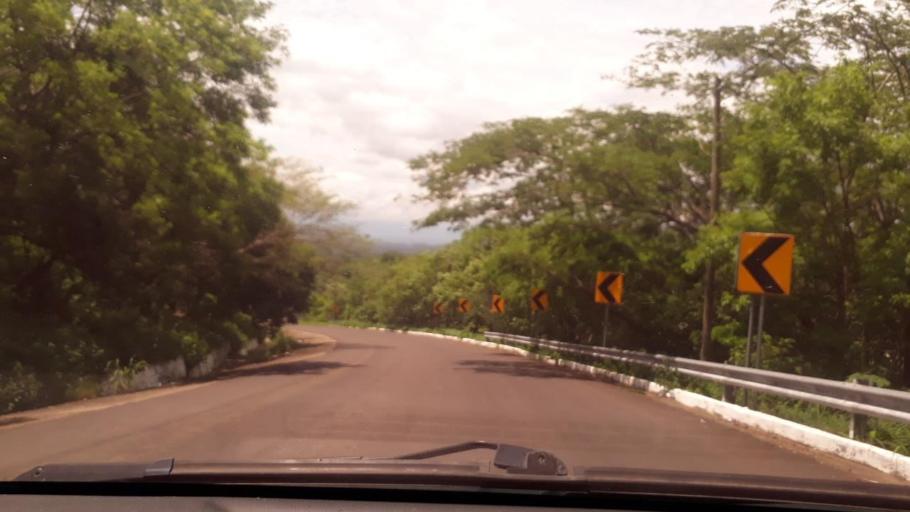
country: GT
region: Jutiapa
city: Jalpatagua
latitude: 14.1666
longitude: -90.0522
